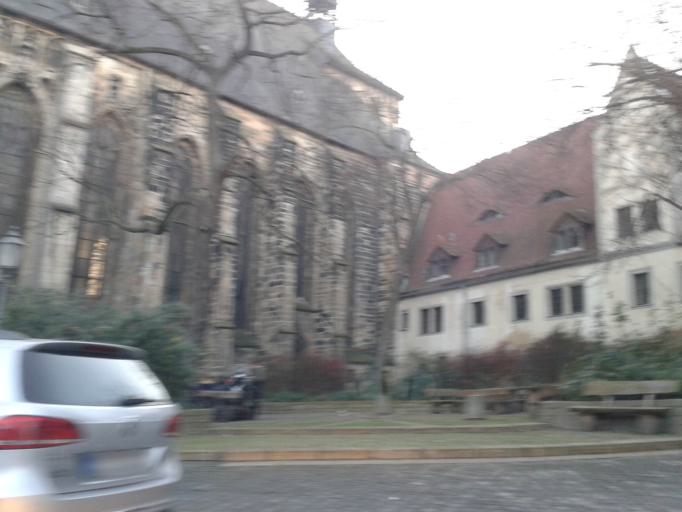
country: DE
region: Saxony-Anhalt
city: Halle (Saale)
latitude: 51.4806
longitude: 11.9666
